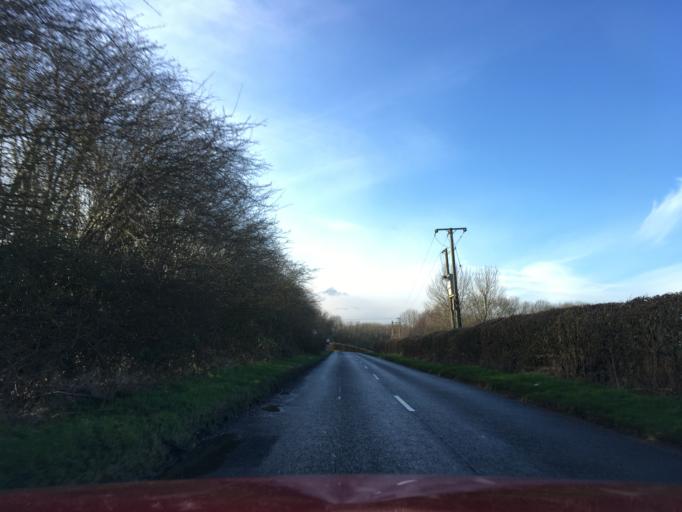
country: GB
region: England
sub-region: Warwickshire
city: Stratford-upon-Avon
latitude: 52.2413
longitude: -1.7187
